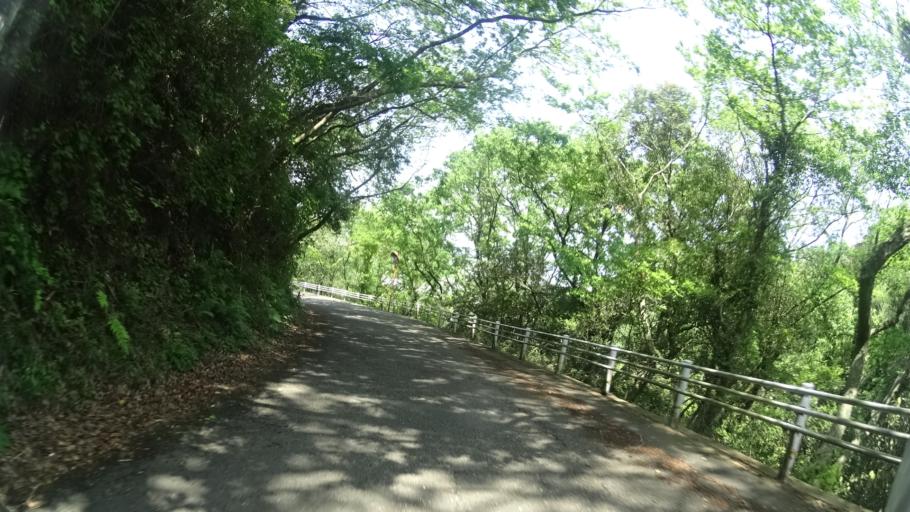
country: JP
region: Tokushima
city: Tokushima-shi
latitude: 34.0665
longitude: 134.5171
